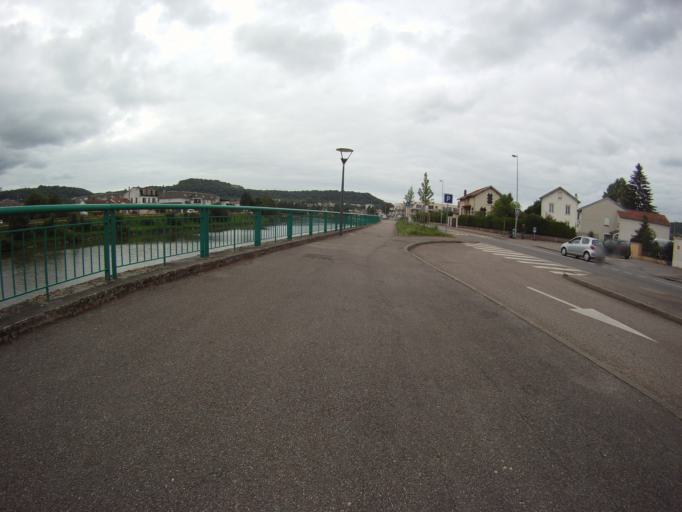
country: FR
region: Lorraine
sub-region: Departement de Meurthe-et-Moselle
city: Malzeville
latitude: 48.7098
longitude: 6.1800
